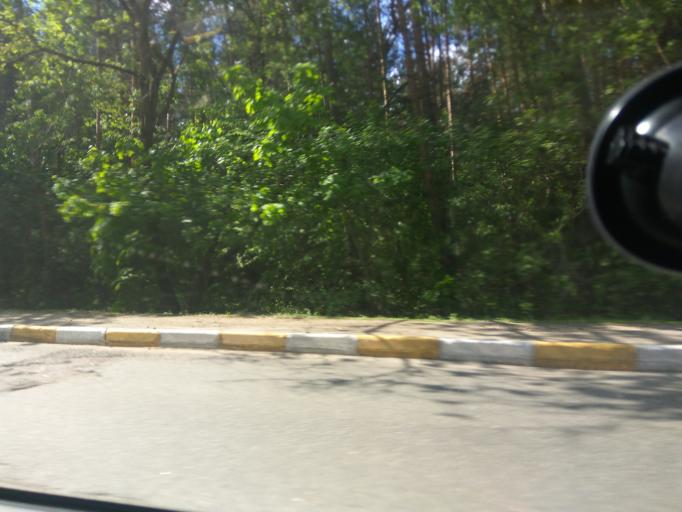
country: RU
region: Moskovskaya
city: Kratovo
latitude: 55.5723
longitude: 38.1730
